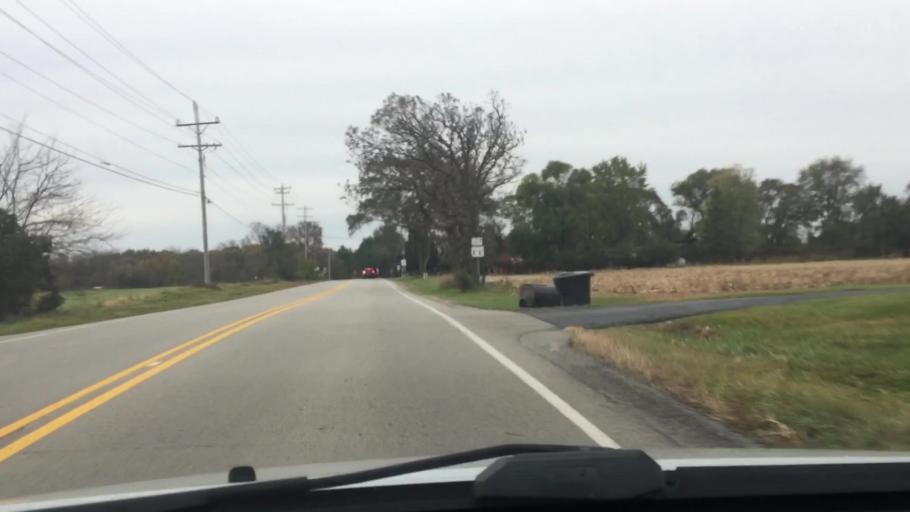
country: US
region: Wisconsin
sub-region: Waukesha County
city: North Prairie
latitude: 42.9098
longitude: -88.4083
